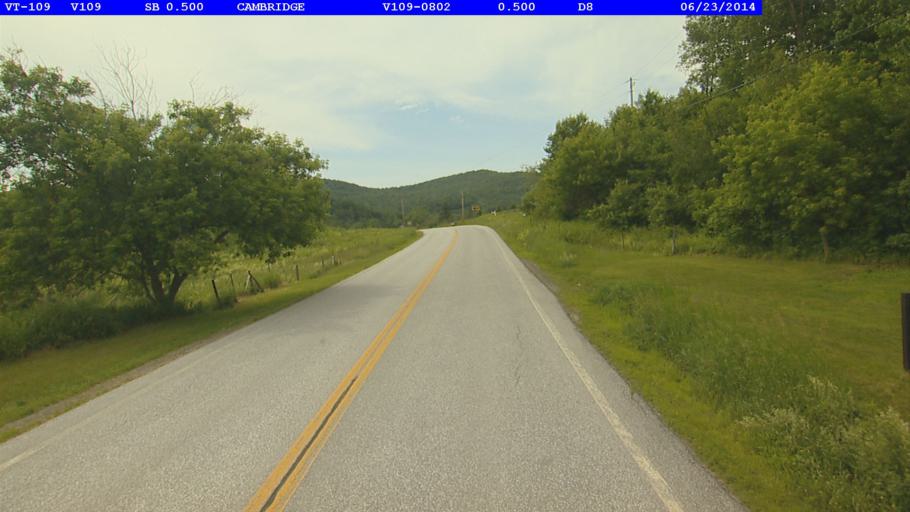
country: US
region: Vermont
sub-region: Lamoille County
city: Johnson
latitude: 44.6539
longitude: -72.8184
